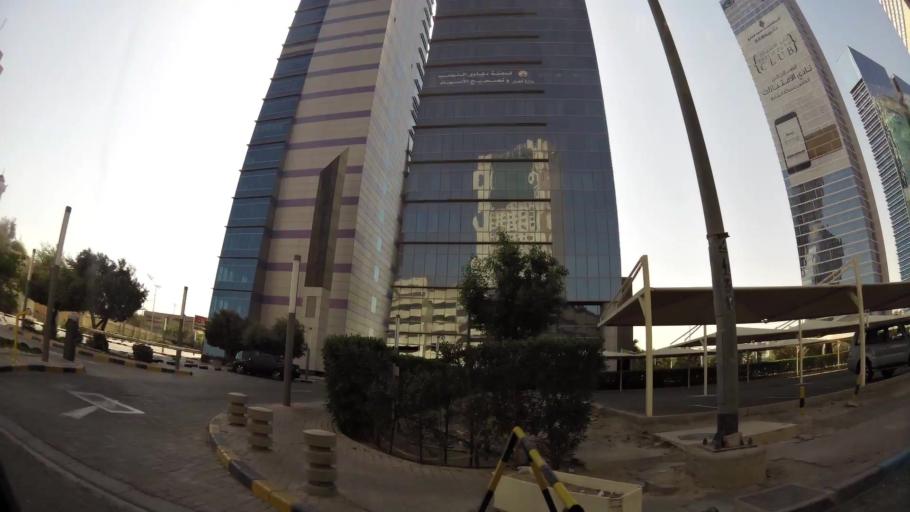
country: KW
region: Al Asimah
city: Kuwait City
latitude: 29.3758
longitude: 47.9909
